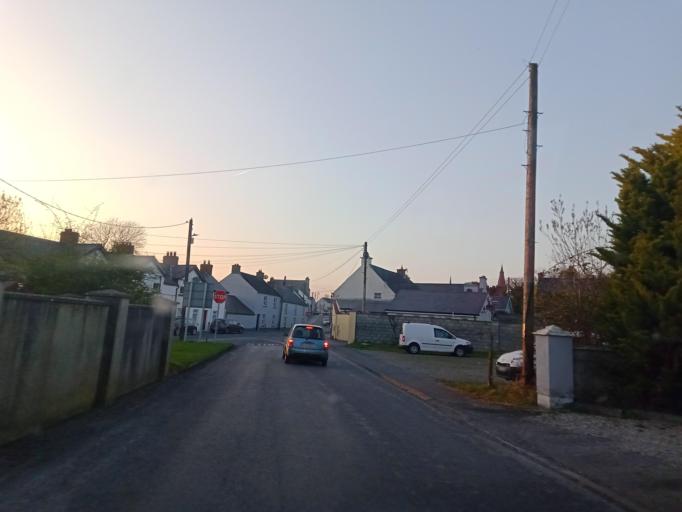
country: IE
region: Leinster
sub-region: Laois
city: Abbeyleix
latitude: 52.8725
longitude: -7.3068
